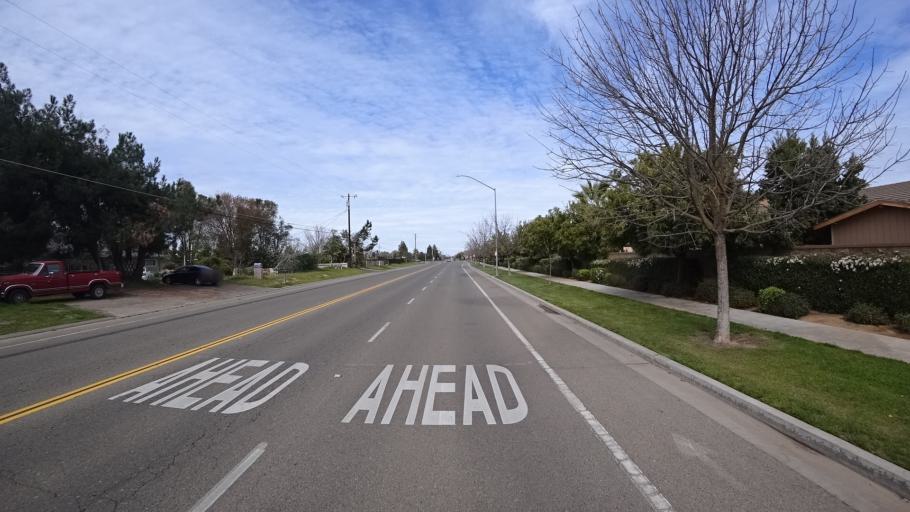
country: US
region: California
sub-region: Fresno County
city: West Park
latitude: 36.7986
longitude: -119.8983
